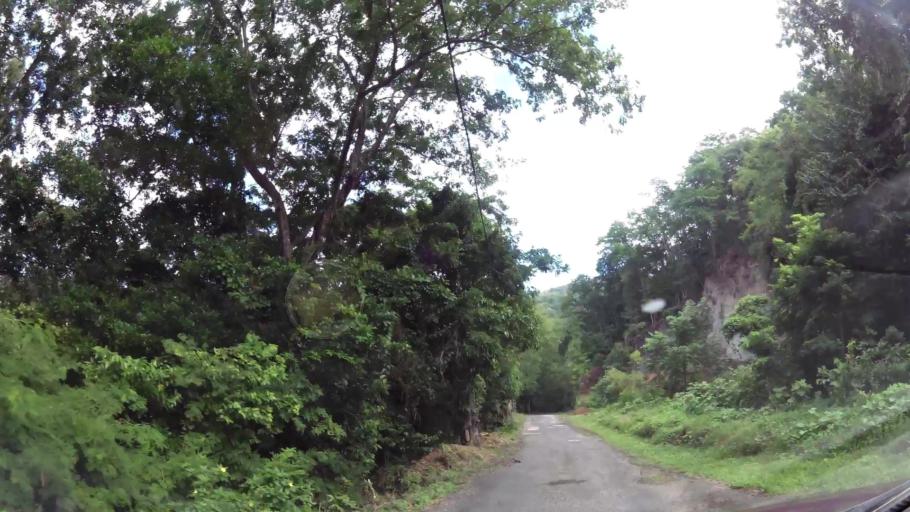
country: DM
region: Saint John
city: Portsmouth
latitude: 15.6183
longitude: -61.4639
